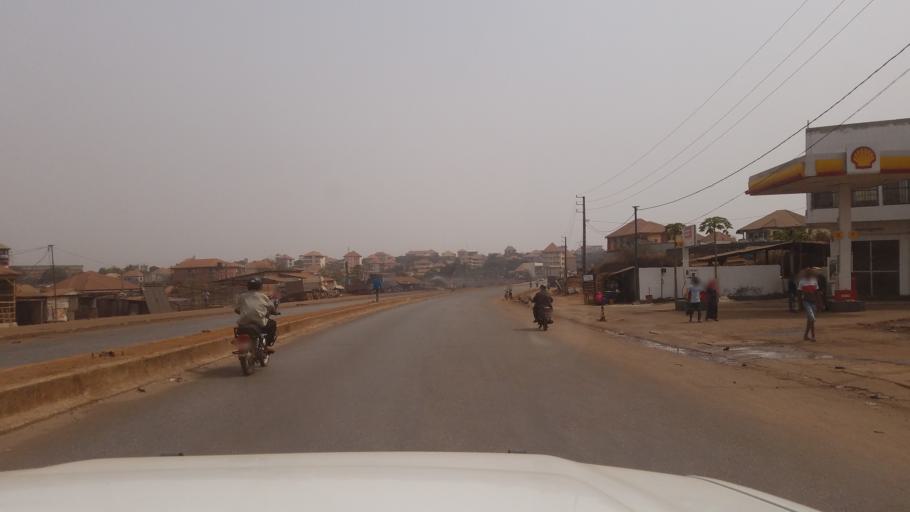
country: GN
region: Kindia
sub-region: Prefecture de Dubreka
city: Dubreka
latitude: 9.6707
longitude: -13.5566
